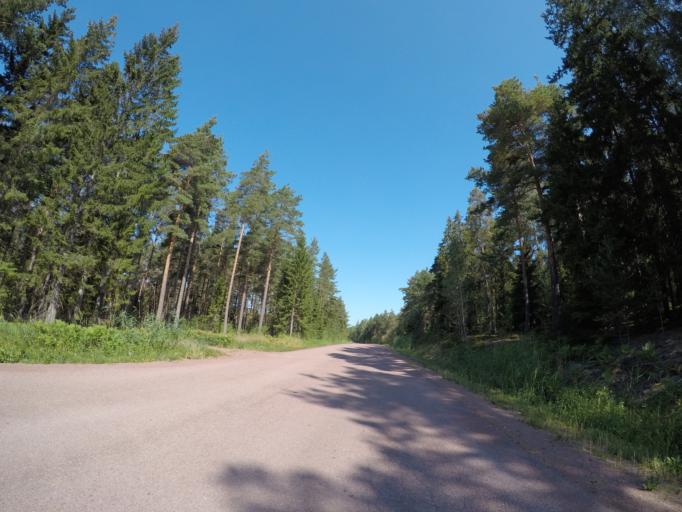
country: AX
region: Alands landsbygd
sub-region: Saltvik
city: Saltvik
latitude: 60.2303
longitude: 20.0072
